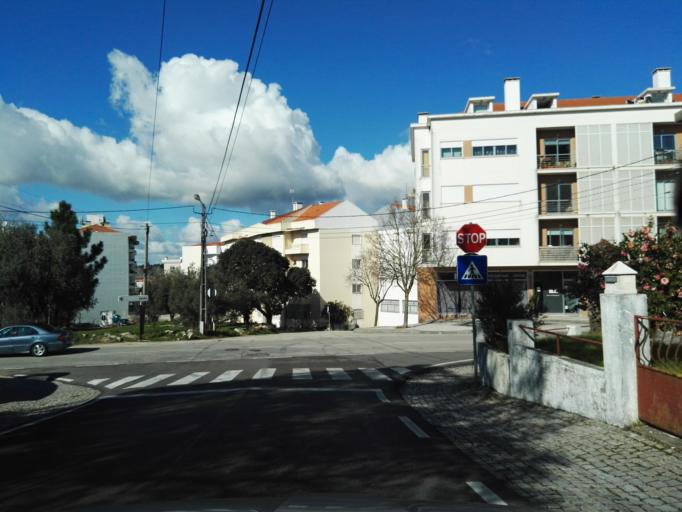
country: PT
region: Santarem
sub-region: Ourem
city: Fatima
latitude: 39.6346
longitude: -8.6789
